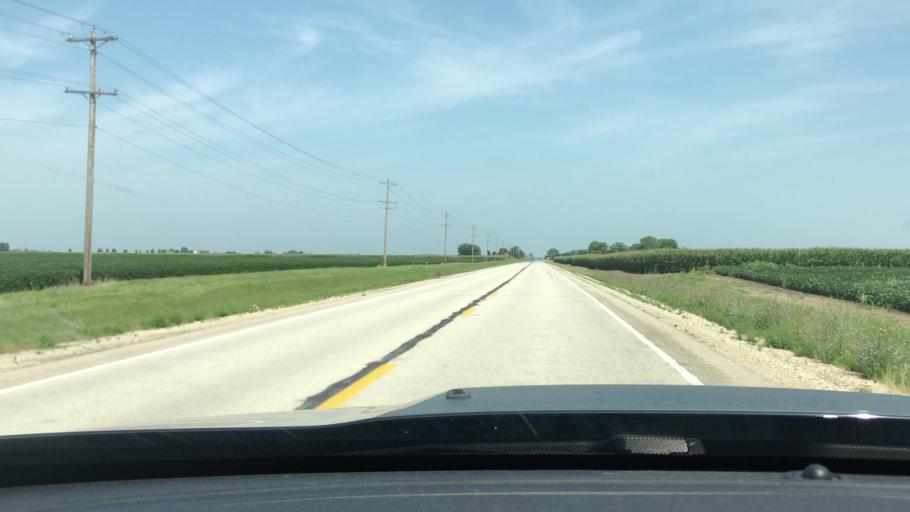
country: US
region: Illinois
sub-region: LaSalle County
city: Ottawa
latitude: 41.4771
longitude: -88.8150
